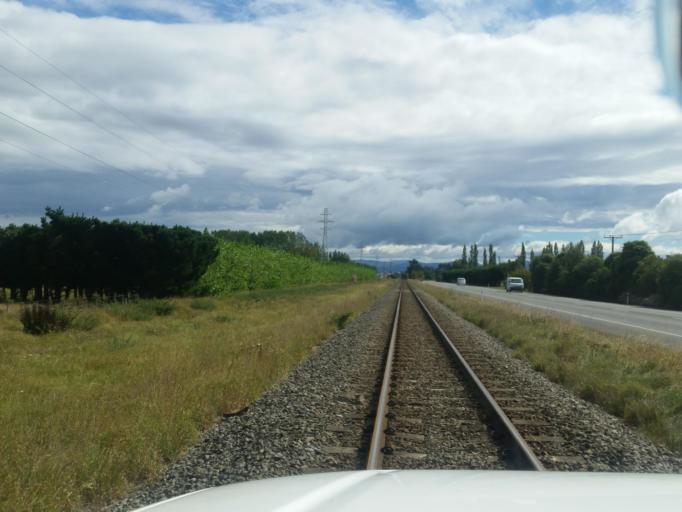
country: NZ
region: Canterbury
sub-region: Waimakariri District
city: Kaiapoi
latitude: -43.3364
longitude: 172.6090
